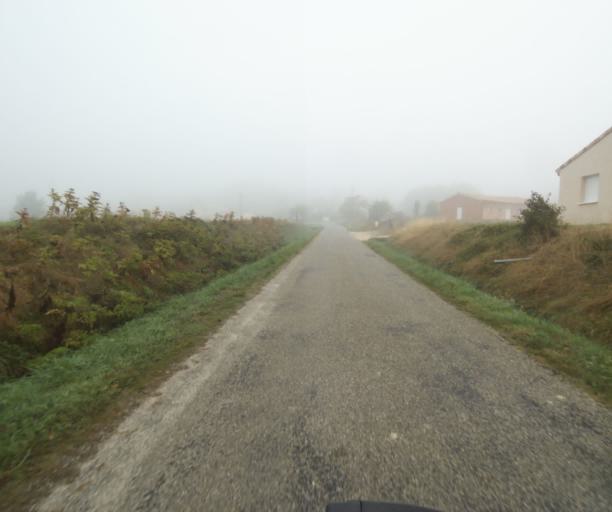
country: FR
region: Midi-Pyrenees
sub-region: Departement de la Haute-Garonne
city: Villemur-sur-Tarn
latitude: 43.9129
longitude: 1.4825
